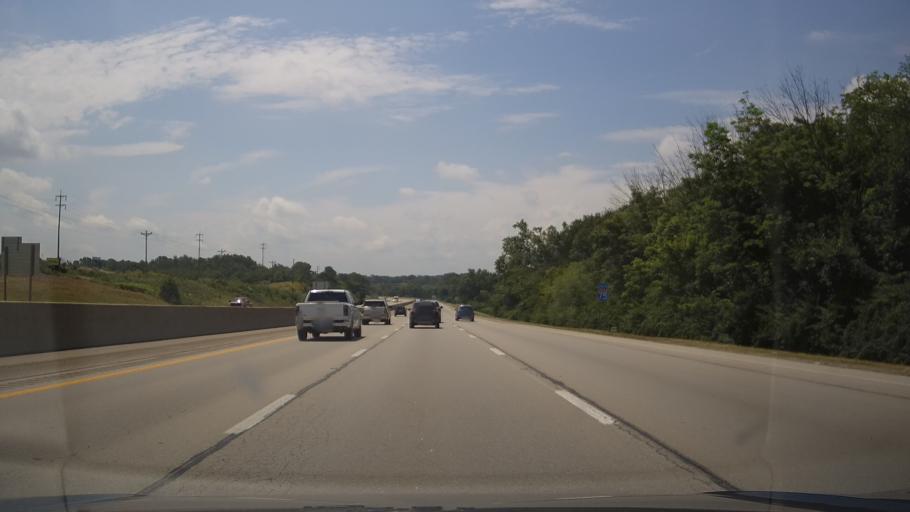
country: US
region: Kentucky
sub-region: Boone County
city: Walton
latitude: 38.8538
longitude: -84.6226
